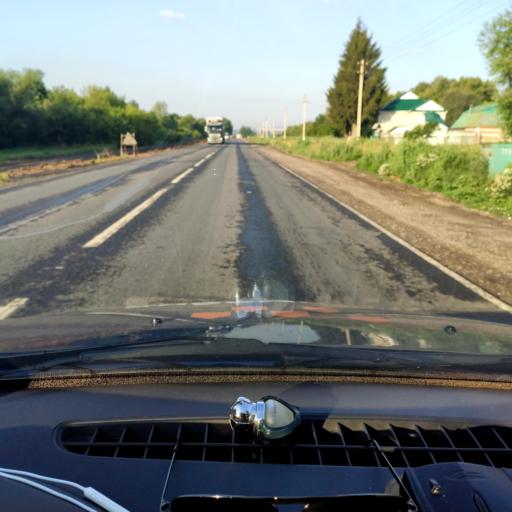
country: RU
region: Lipetsk
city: Kazaki
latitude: 52.5084
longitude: 38.0933
